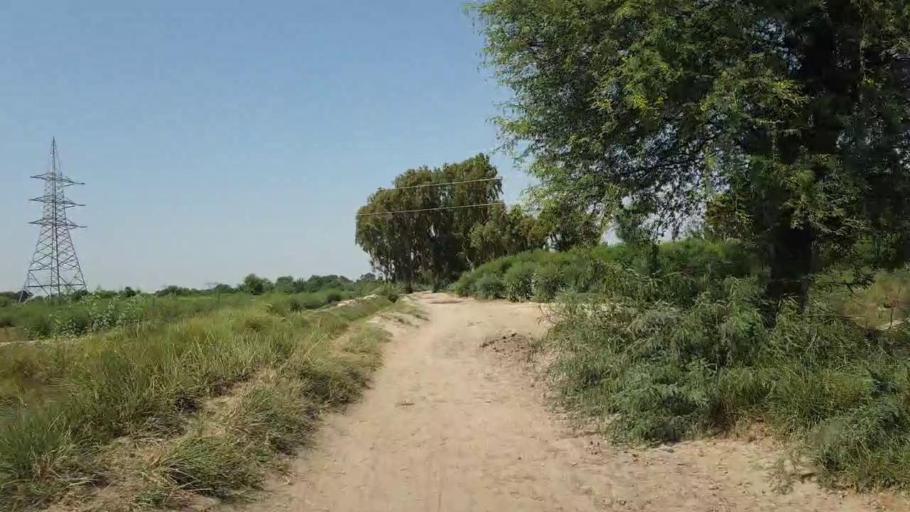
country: PK
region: Sindh
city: Hyderabad
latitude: 25.4764
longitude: 68.4149
